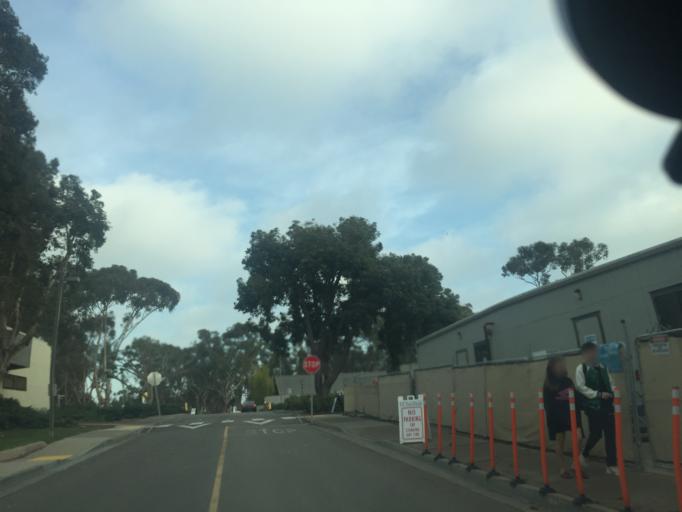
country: US
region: California
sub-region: San Diego County
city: La Jolla
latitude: 32.8797
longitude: -117.2407
